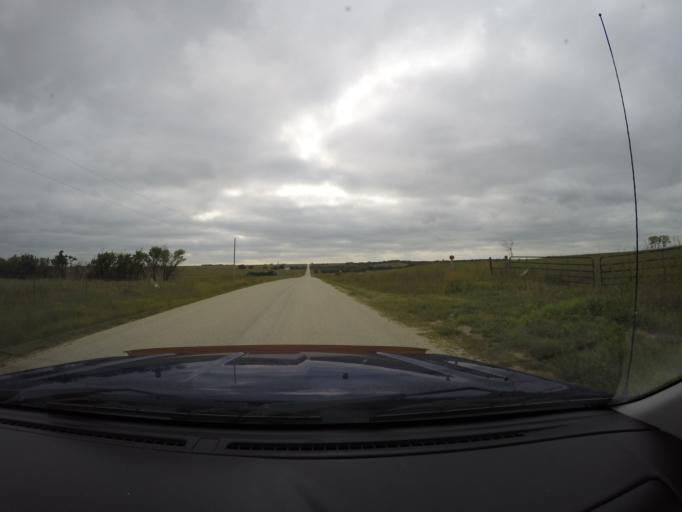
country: US
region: Kansas
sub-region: Dickinson County
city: Herington
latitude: 38.7974
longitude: -96.7921
